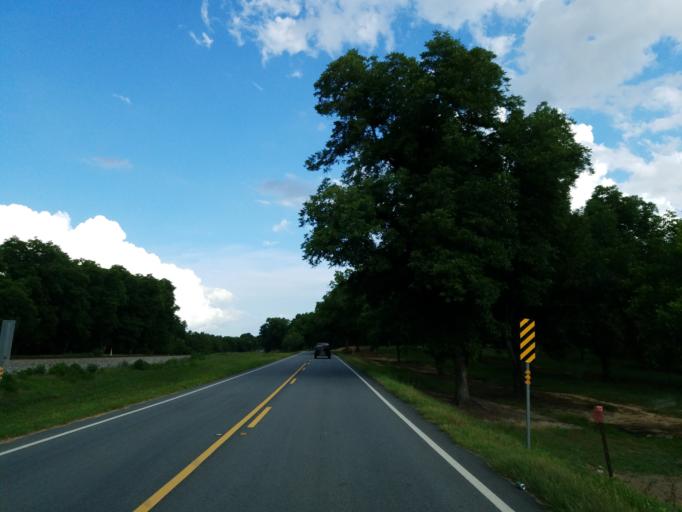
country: US
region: Georgia
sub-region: Turner County
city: Ashburn
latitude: 31.7888
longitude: -83.7048
